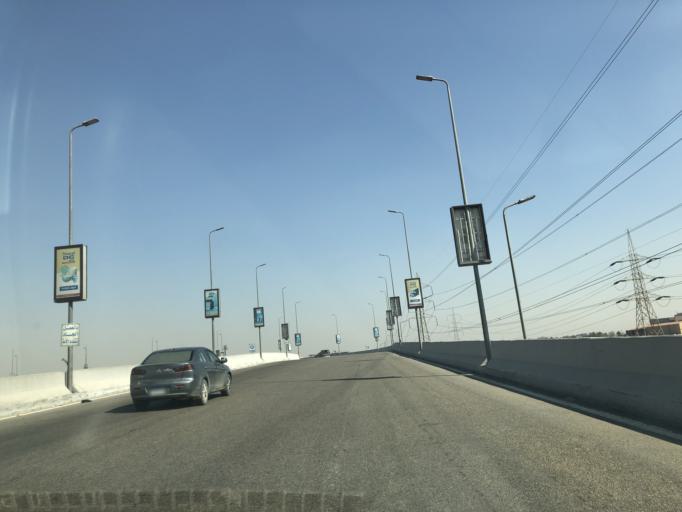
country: EG
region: Al Jizah
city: Madinat Sittah Uktubar
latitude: 29.9709
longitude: 31.0109
